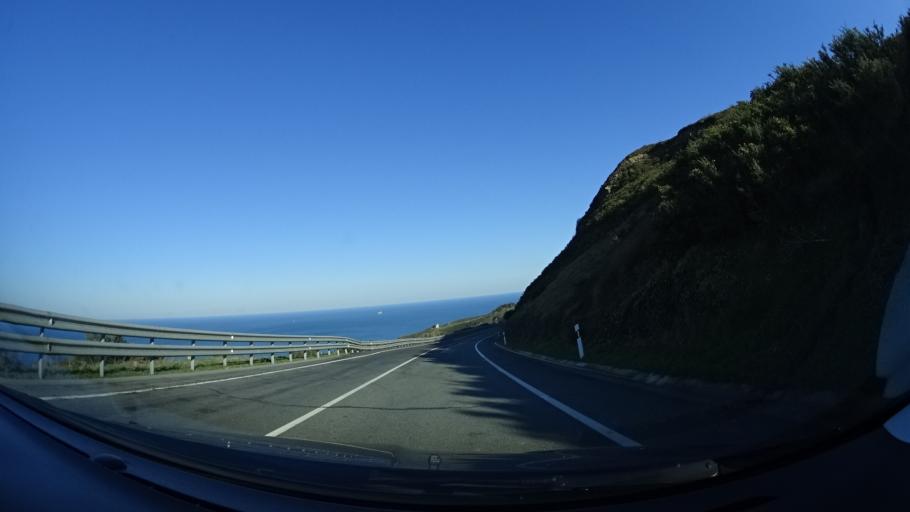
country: ES
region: Basque Country
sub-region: Bizkaia
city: Bakio
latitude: 43.4430
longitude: -2.7650
